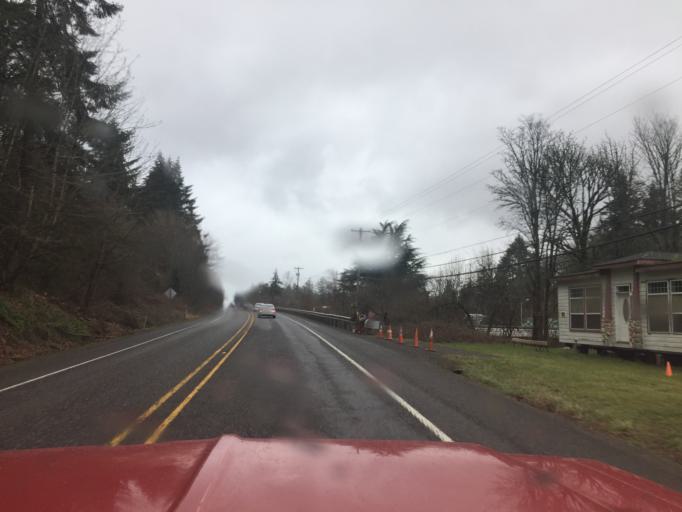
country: US
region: Oregon
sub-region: Columbia County
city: Rainier
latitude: 46.0654
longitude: -122.8971
